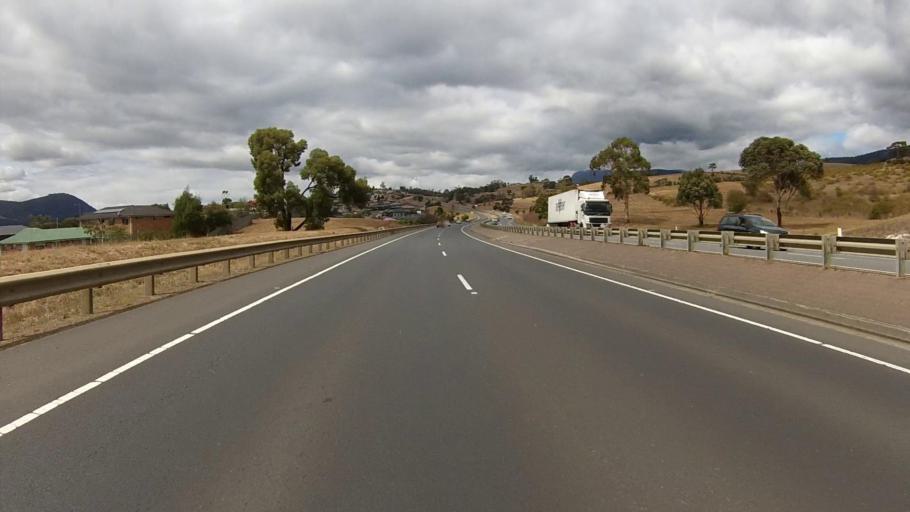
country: AU
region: Tasmania
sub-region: Glenorchy
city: Granton
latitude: -42.7628
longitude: 147.2346
